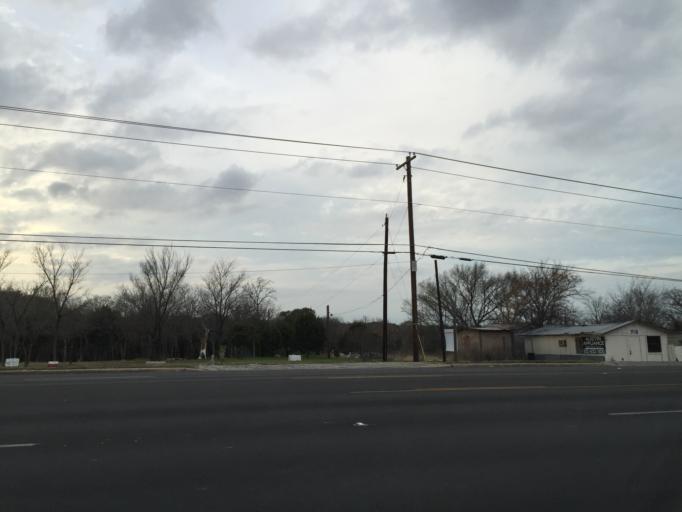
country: US
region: Texas
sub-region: Travis County
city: Wells Branch
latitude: 30.3860
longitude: -97.6842
